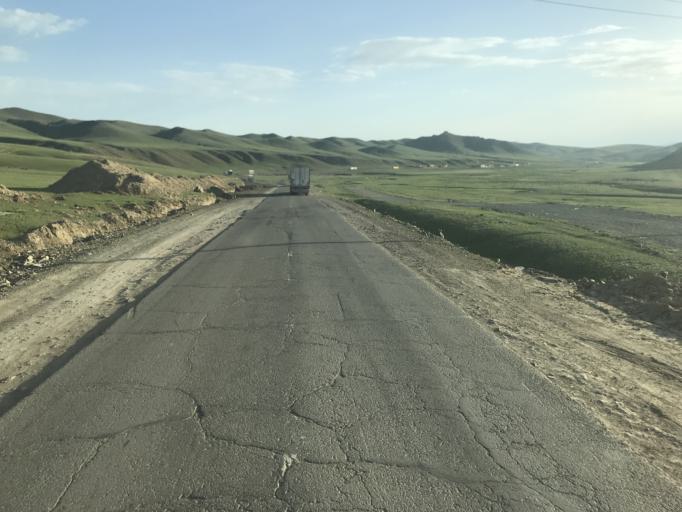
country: MN
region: Central Aimak
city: Bornuur
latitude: 48.4320
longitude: 106.1931
